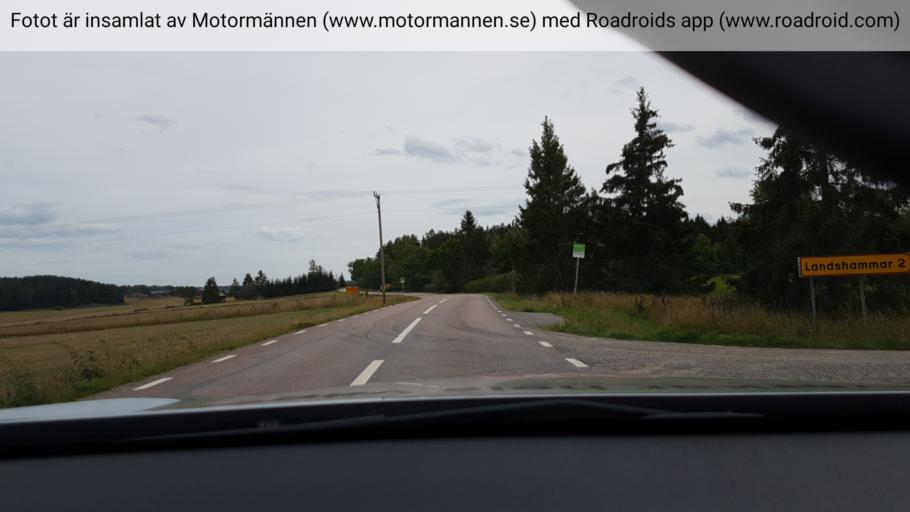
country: SE
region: Soedermanland
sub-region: Nykopings Kommun
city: Nykoping
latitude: 58.9009
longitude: 17.0932
